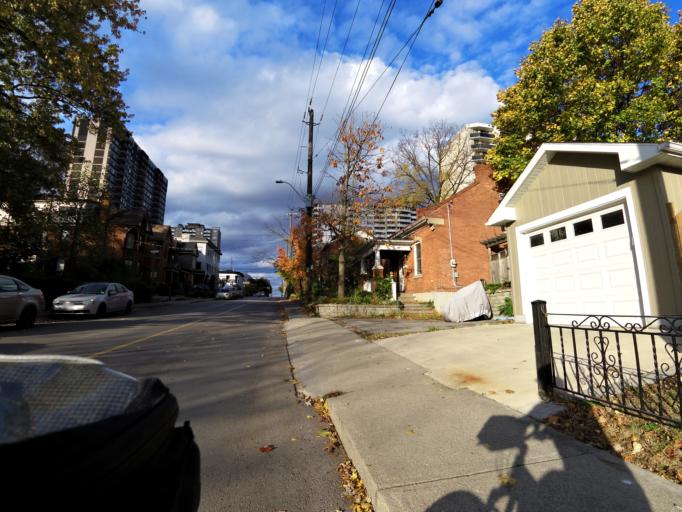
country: CA
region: Ontario
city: Hamilton
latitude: 43.2535
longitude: -79.8779
